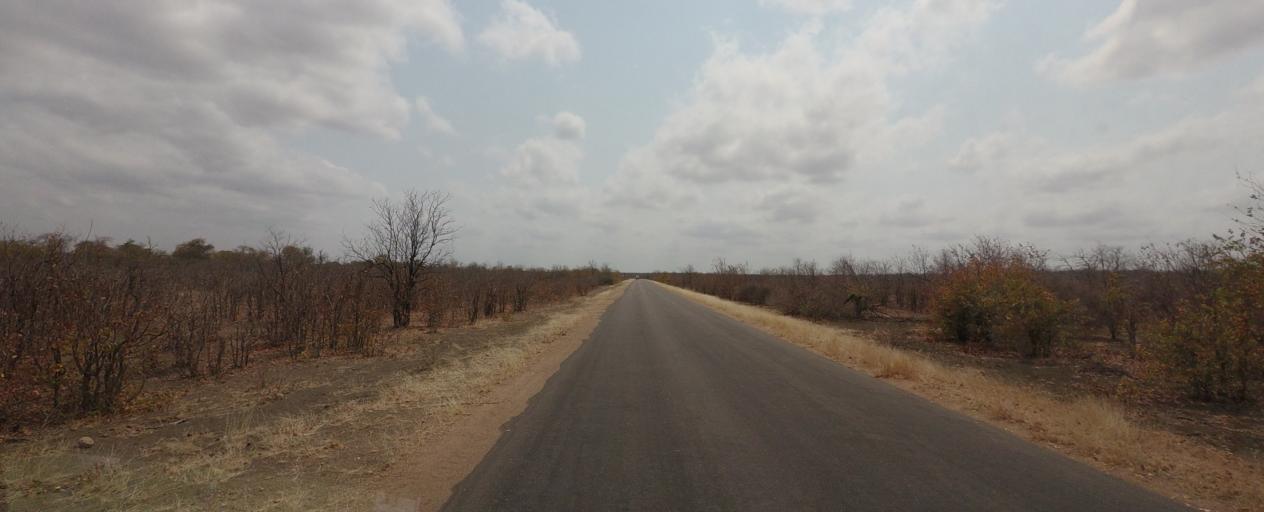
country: ZA
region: Limpopo
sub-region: Mopani District Municipality
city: Phalaborwa
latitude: -23.6041
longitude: 31.4546
